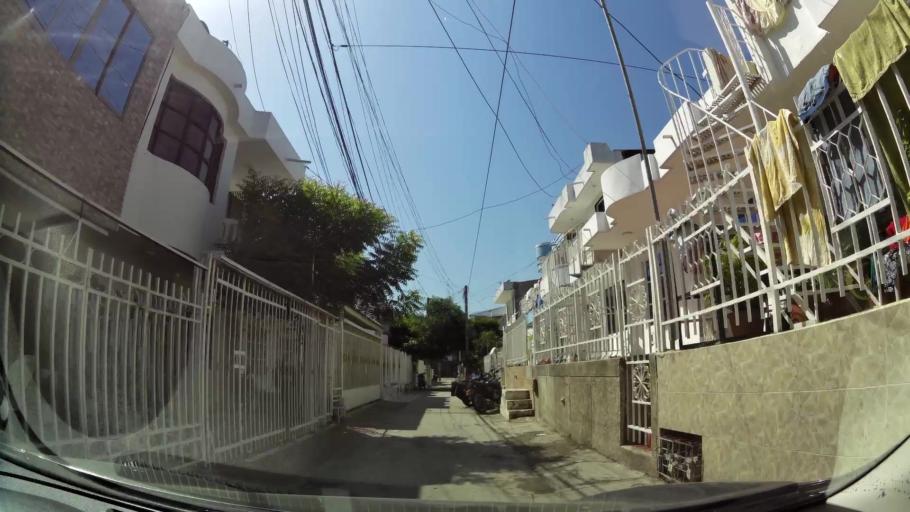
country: CO
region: Bolivar
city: Cartagena
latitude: 10.3885
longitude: -75.5081
